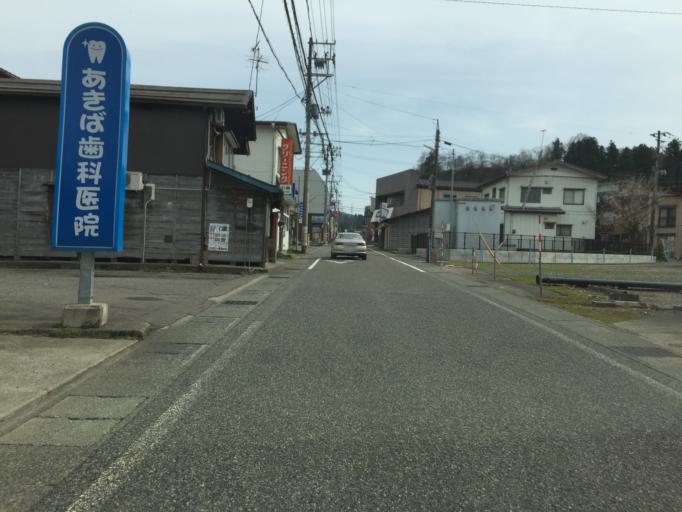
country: JP
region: Niigata
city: Tochio-honcho
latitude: 37.4697
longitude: 139.0032
